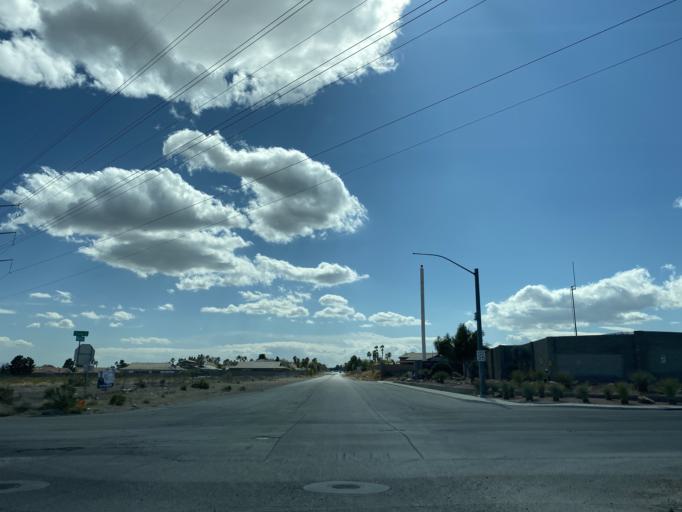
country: US
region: Nevada
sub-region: Clark County
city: Summerlin South
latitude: 36.2412
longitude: -115.2884
